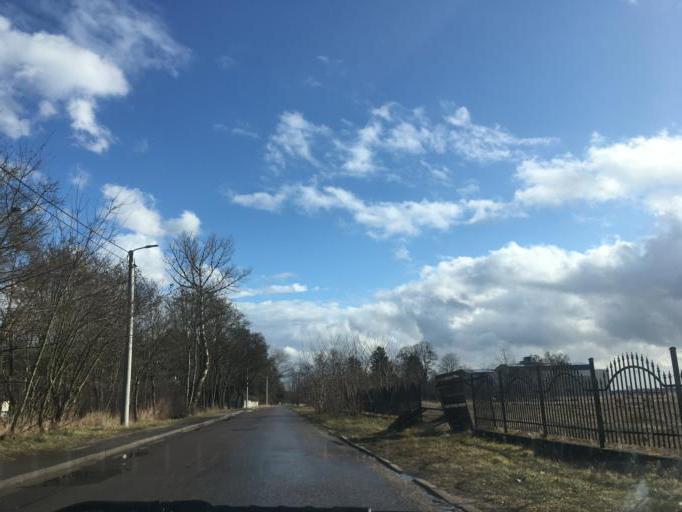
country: PL
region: Pomeranian Voivodeship
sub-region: Powiat gdanski
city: Cedry Wielkie
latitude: 54.3486
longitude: 18.8072
